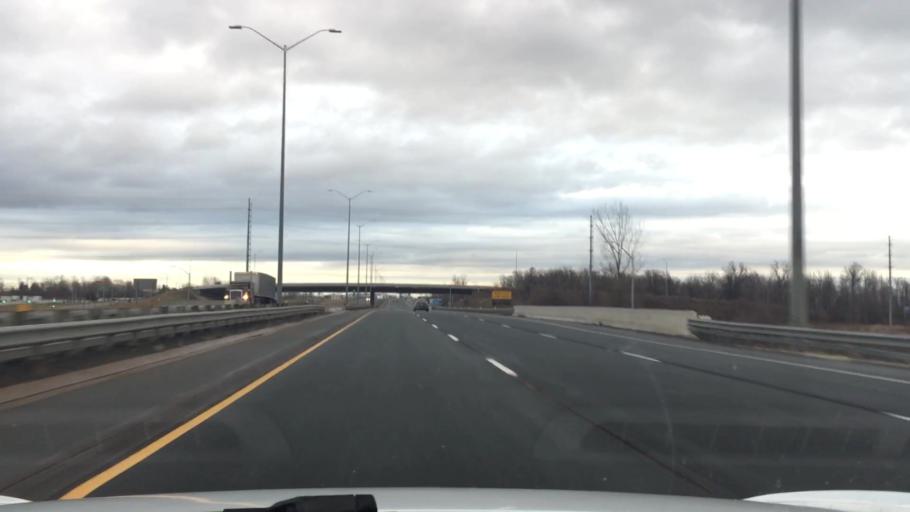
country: CA
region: Ontario
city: Fort Erie
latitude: 42.9120
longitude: -78.9446
